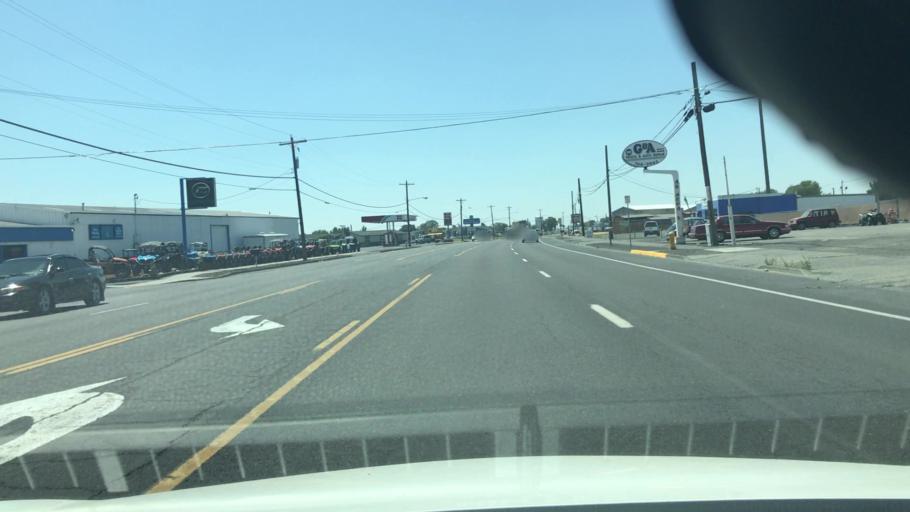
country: US
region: Washington
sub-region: Grant County
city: Moses Lake
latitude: 47.1151
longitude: -119.2971
